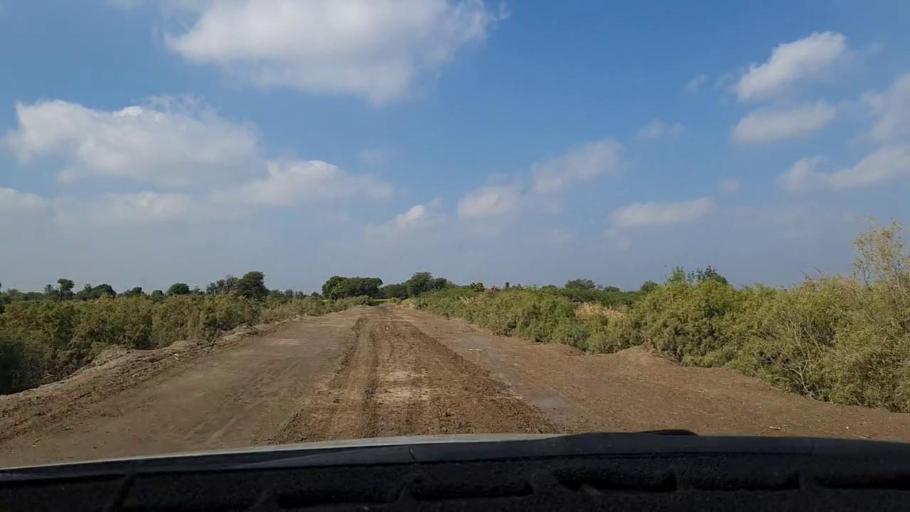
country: PK
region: Sindh
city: Tando Mittha Khan
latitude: 25.7759
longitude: 69.2568
